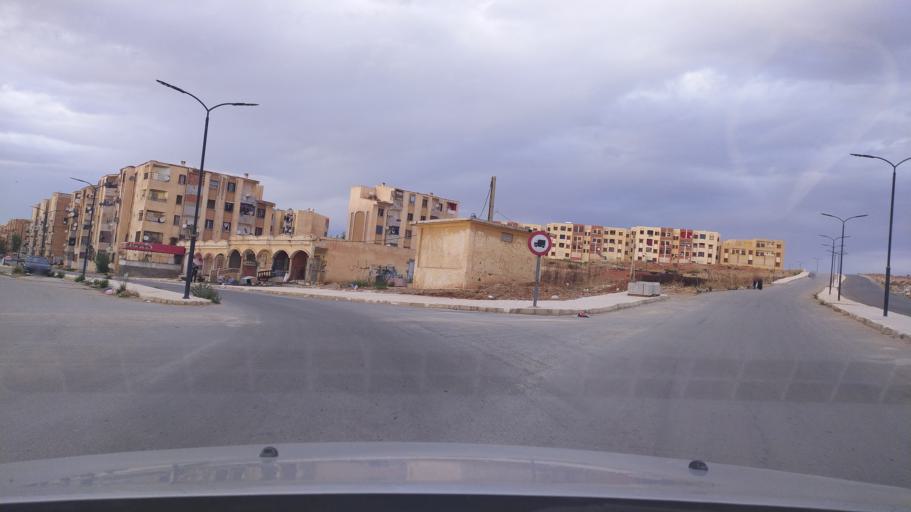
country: DZ
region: Tiaret
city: Frenda
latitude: 35.0543
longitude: 1.0626
